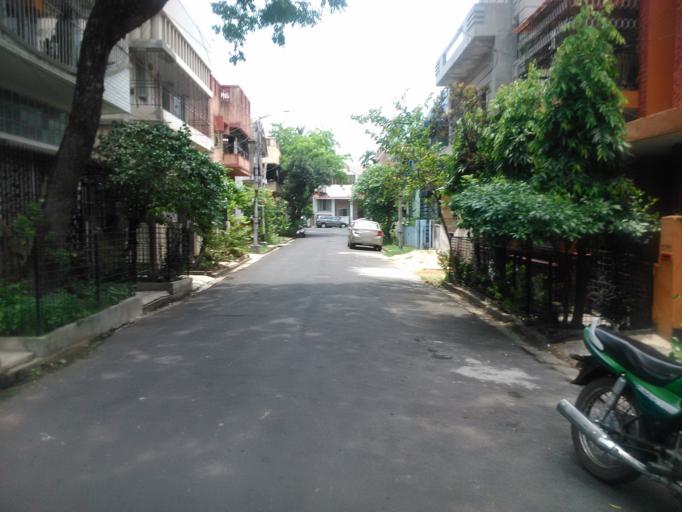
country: IN
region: West Bengal
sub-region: North 24 Parganas
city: Garui
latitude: 22.5936
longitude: 88.4066
